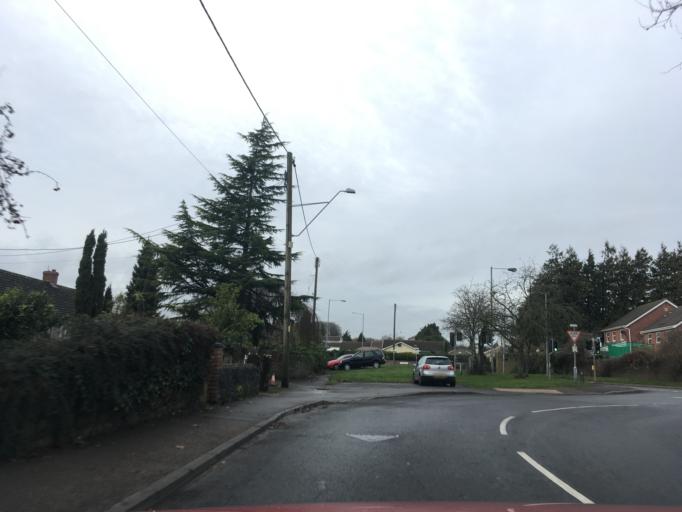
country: GB
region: Wales
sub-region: Monmouthshire
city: Magor
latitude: 51.5817
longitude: -2.8321
